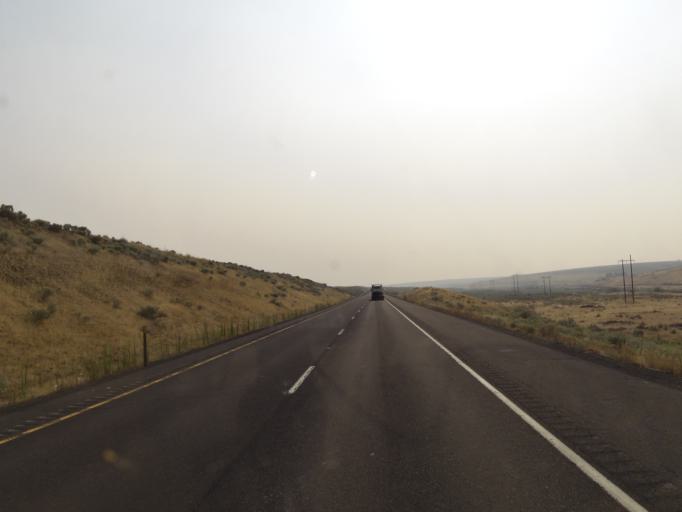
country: US
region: Washington
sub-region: Adams County
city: Ritzville
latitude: 47.0119
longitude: -118.5118
